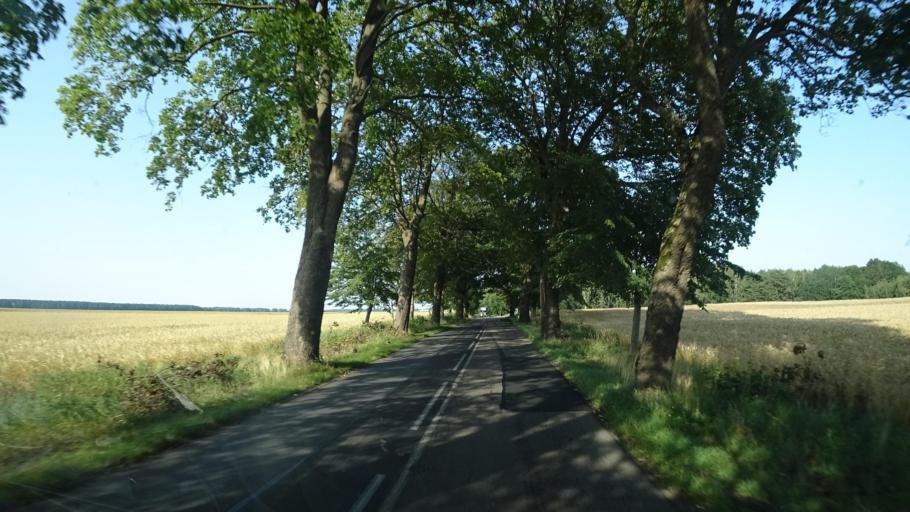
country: PL
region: Pomeranian Voivodeship
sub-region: Powiat czluchowski
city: Przechlewo
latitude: 53.8124
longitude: 17.3550
